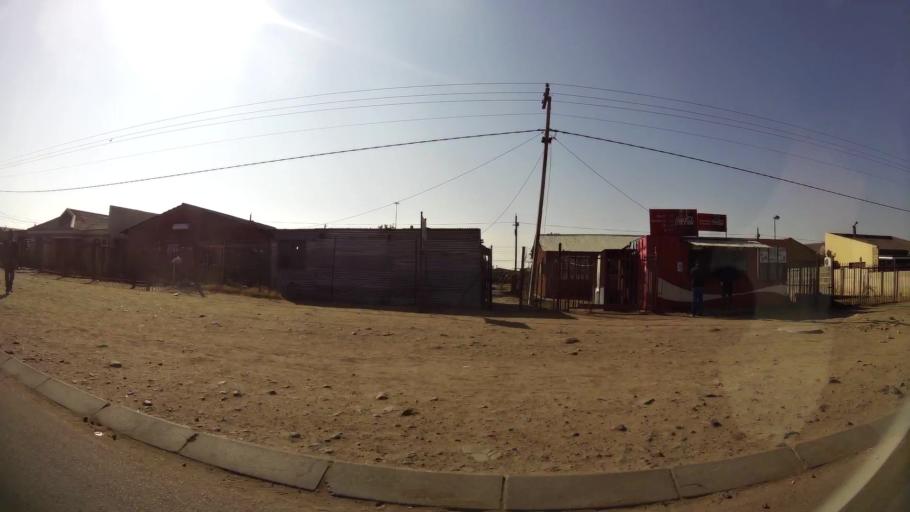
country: ZA
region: Orange Free State
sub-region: Mangaung Metropolitan Municipality
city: Bloemfontein
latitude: -29.1828
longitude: 26.2439
